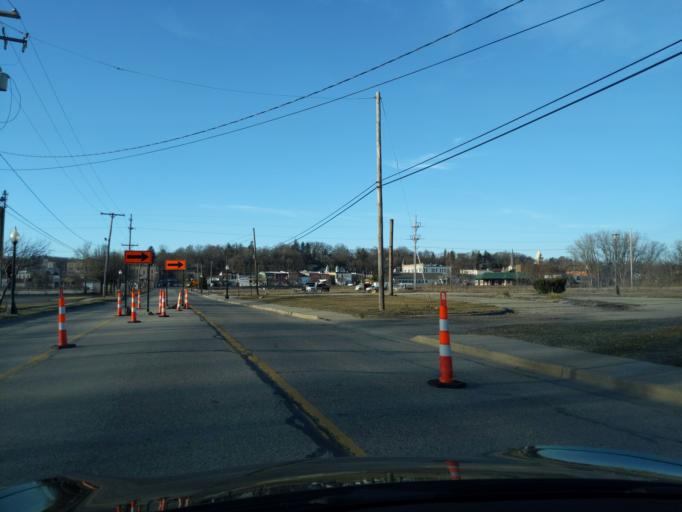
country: US
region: Michigan
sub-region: Ionia County
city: Ionia
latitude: 42.9784
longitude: -85.0673
